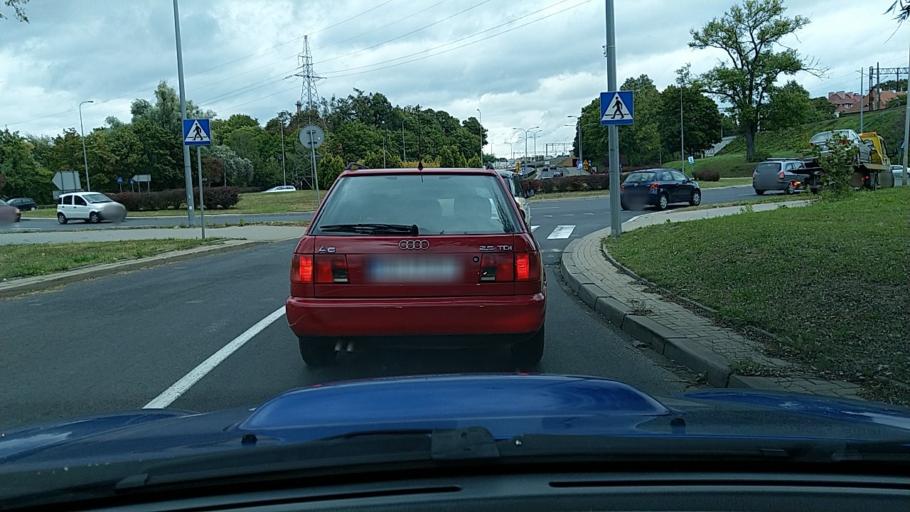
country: PL
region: Warmian-Masurian Voivodeship
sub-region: Olsztyn
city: Kortowo
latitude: 53.7777
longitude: 20.4629
